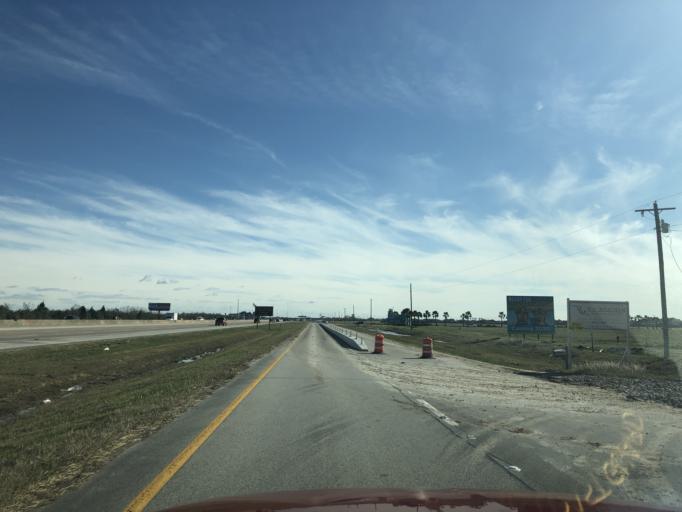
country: US
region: Texas
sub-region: Galveston County
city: Dickinson
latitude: 29.4189
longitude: -95.0495
